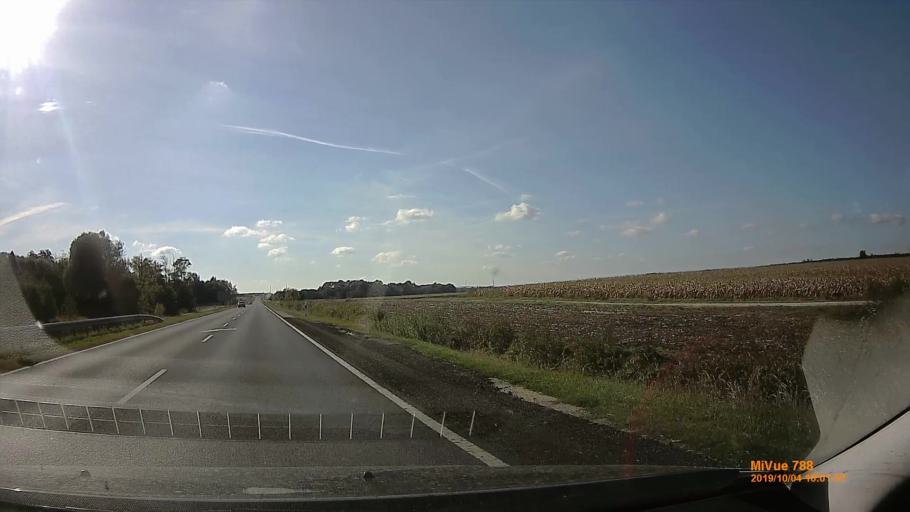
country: HU
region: Somogy
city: Kaposvar
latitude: 46.4117
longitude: 17.7704
